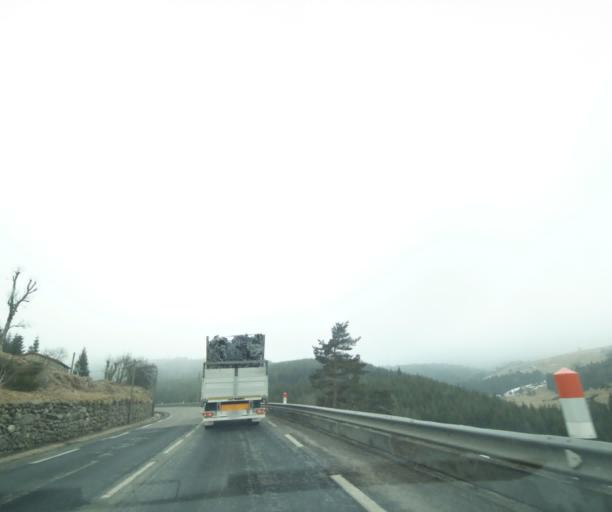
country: FR
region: Languedoc-Roussillon
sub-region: Departement de la Lozere
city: Langogne
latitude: 44.7116
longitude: 4.0079
